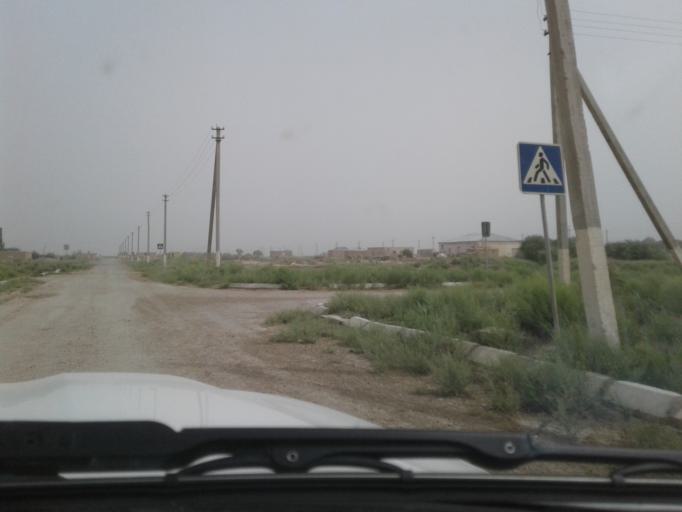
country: TM
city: Akdepe
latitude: 41.5970
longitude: 58.6082
